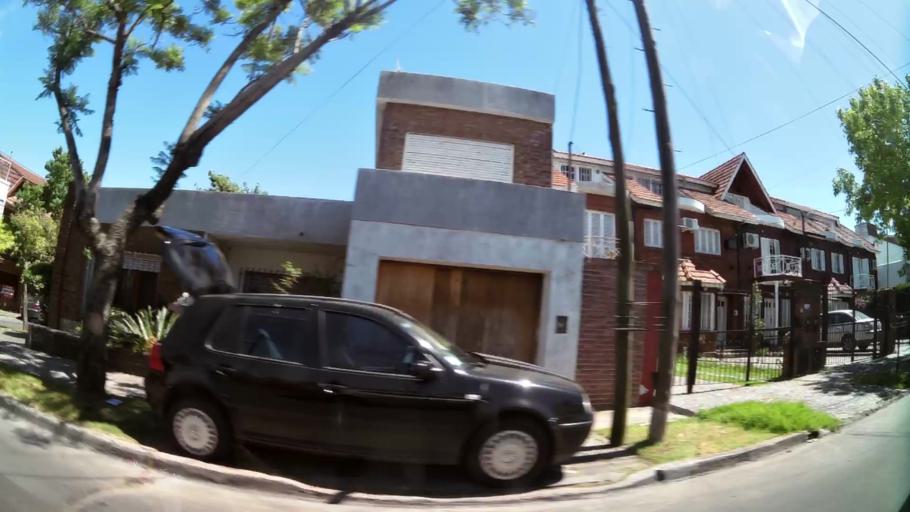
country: AR
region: Buenos Aires
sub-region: Partido de San Isidro
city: San Isidro
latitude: -34.4728
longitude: -58.5280
